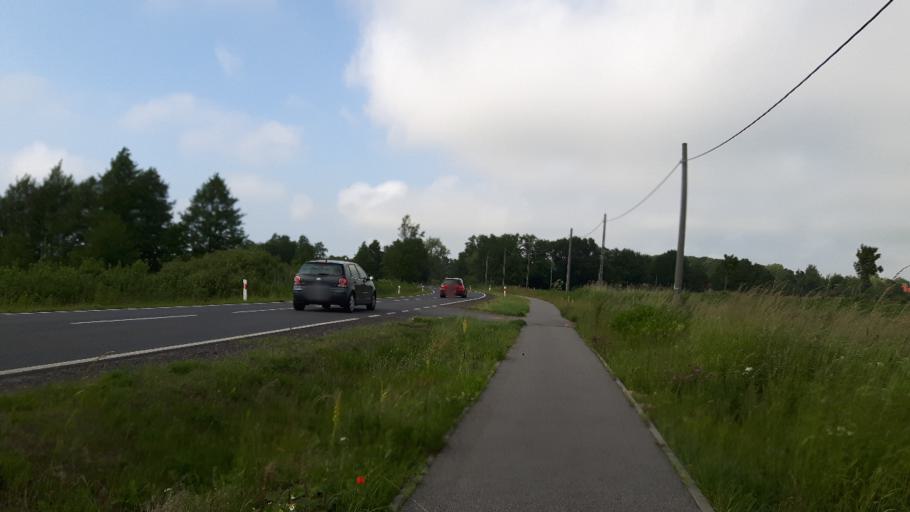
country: PL
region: West Pomeranian Voivodeship
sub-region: Powiat slawienski
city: Darlowo
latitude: 54.3483
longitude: 16.3324
